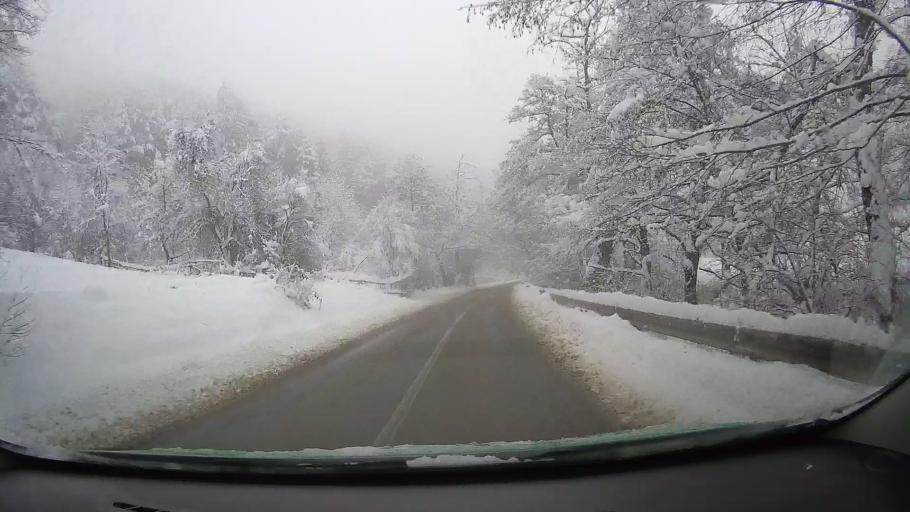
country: RO
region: Sibiu
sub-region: Comuna Tilisca
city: Tilisca
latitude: 45.8043
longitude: 23.8277
